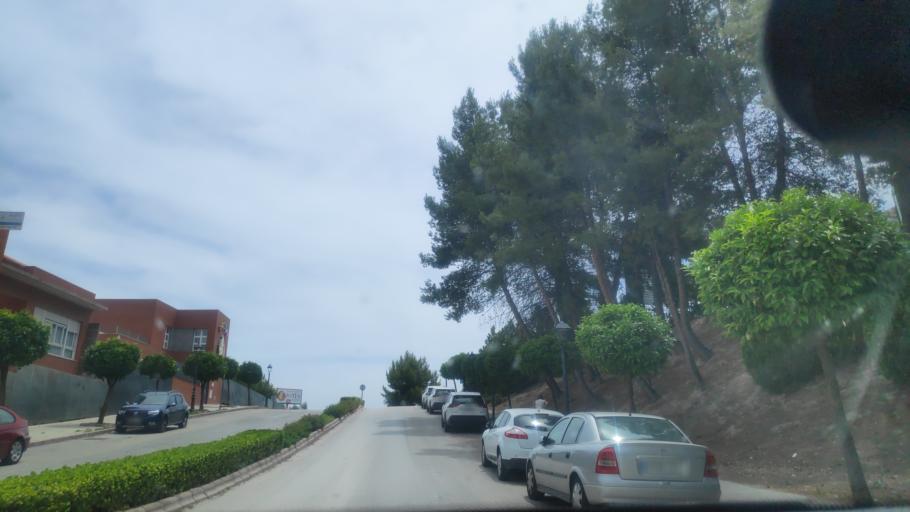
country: ES
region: Andalusia
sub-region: Provincia de Jaen
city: Jaen
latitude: 37.7793
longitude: -3.8117
